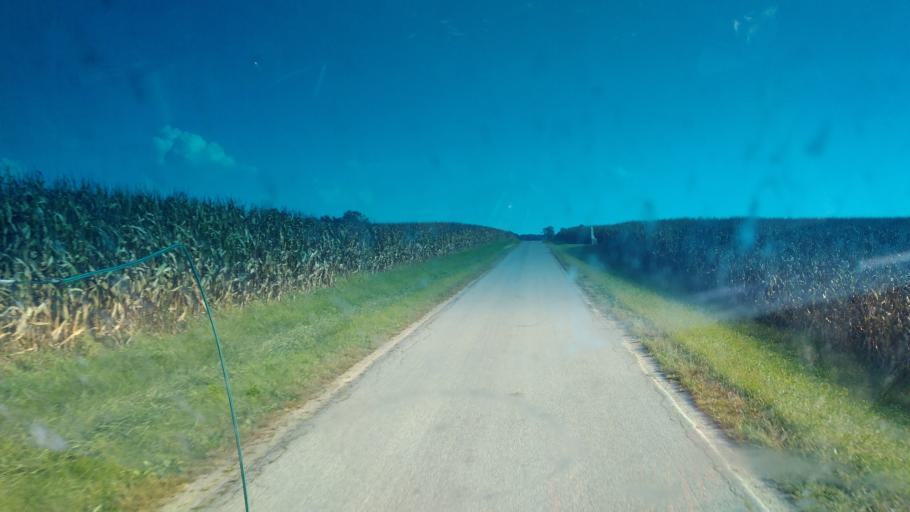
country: US
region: Ohio
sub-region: Wyandot County
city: Upper Sandusky
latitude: 40.8962
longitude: -83.2438
